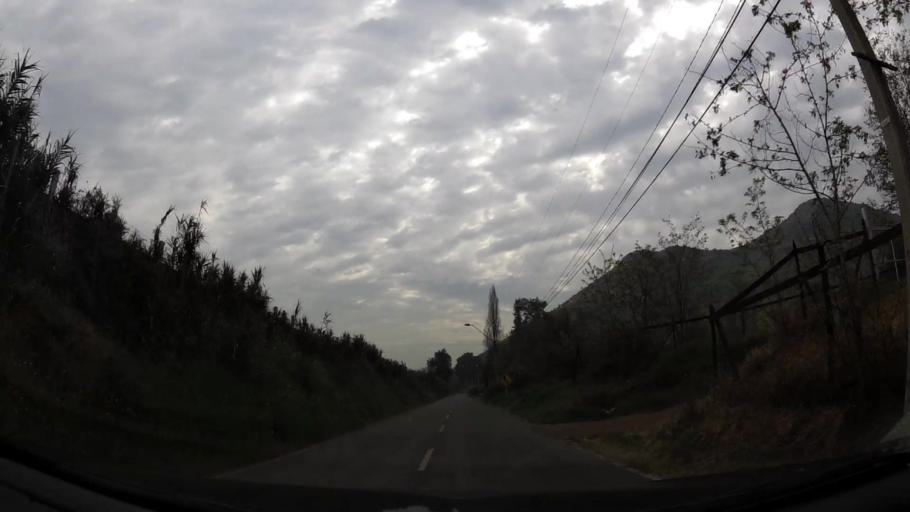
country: CL
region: Santiago Metropolitan
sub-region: Provincia de Chacabuco
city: Chicureo Abajo
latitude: -33.2435
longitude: -70.6749
